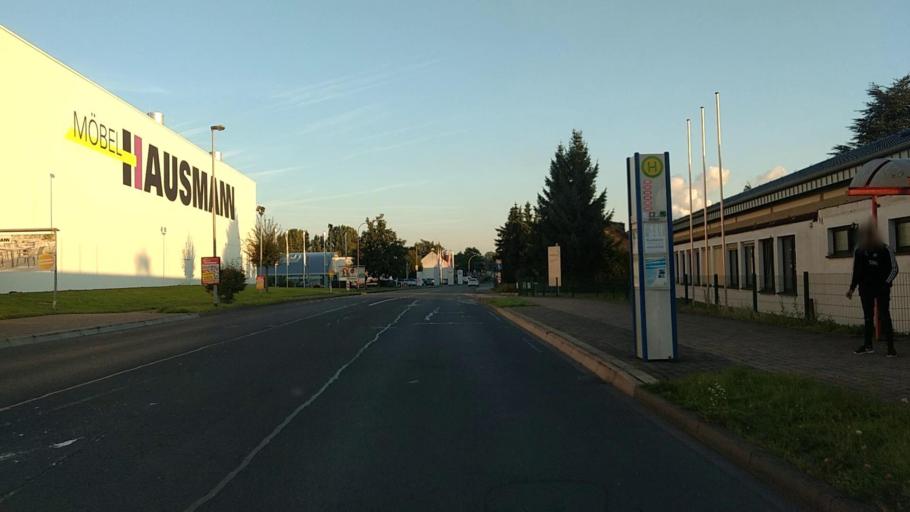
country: DE
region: North Rhine-Westphalia
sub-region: Regierungsbezirk Koln
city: Bergheim
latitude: 50.9471
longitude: 6.6269
